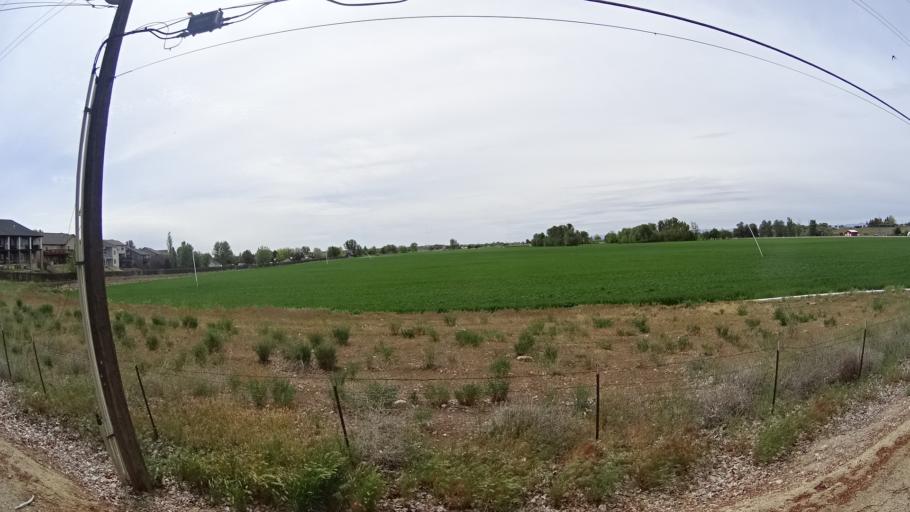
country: US
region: Idaho
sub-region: Ada County
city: Kuna
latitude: 43.5321
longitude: -116.3307
